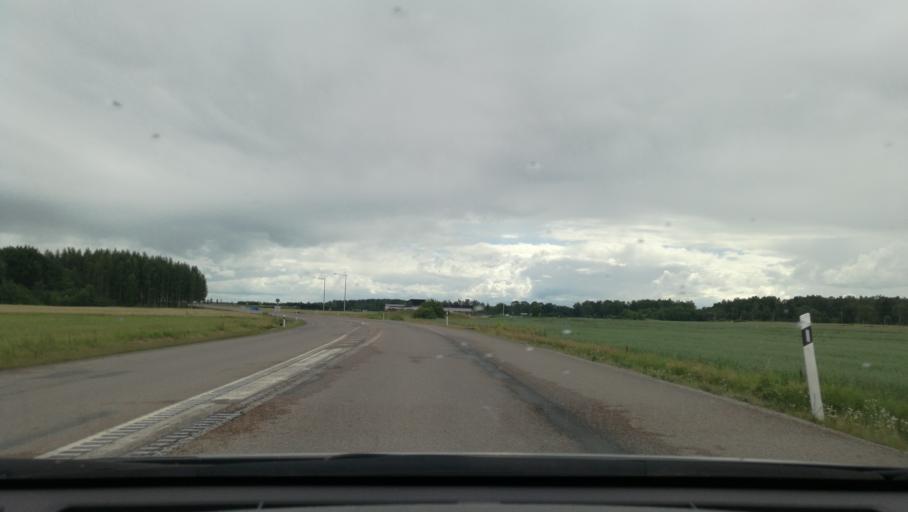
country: SE
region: Vaestmanland
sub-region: Kopings Kommun
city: Koping
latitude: 59.4858
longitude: 15.9851
